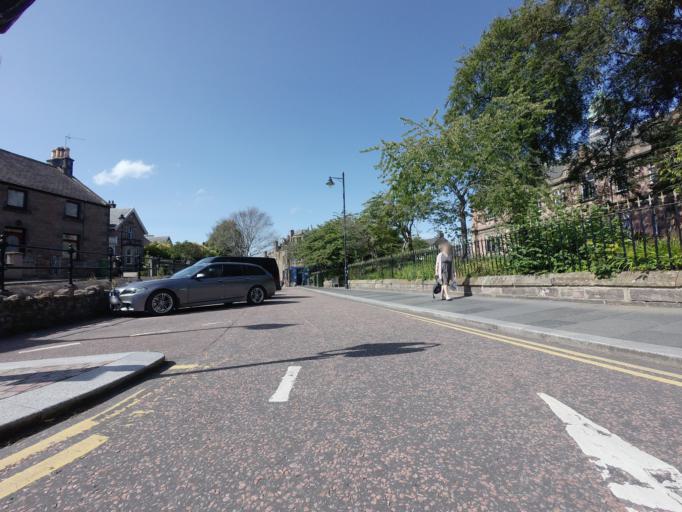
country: GB
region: Scotland
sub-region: Highland
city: Inverness
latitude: 57.4775
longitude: -4.2189
